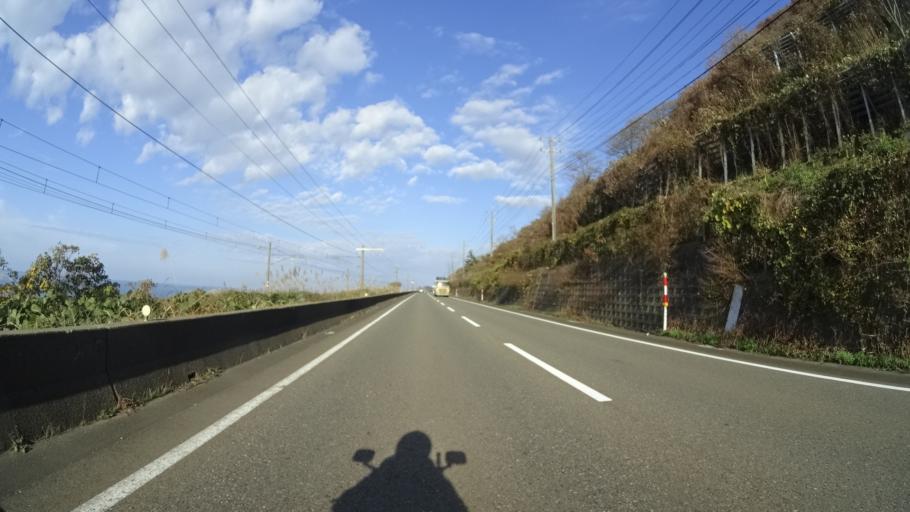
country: JP
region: Niigata
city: Kashiwazaki
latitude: 37.2996
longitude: 138.4115
